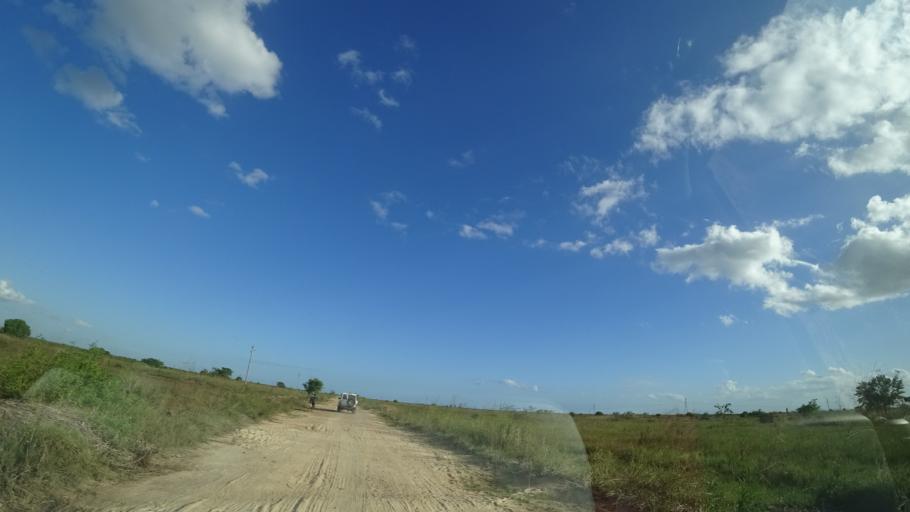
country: MZ
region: Sofala
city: Dondo
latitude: -19.4509
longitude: 34.5625
